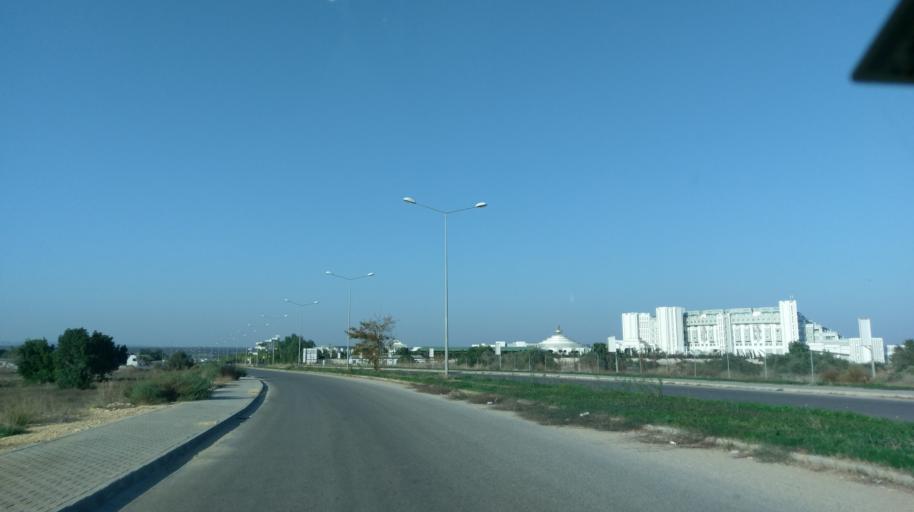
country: CY
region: Ammochostos
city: Leonarisso
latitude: 35.3599
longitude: 34.0712
